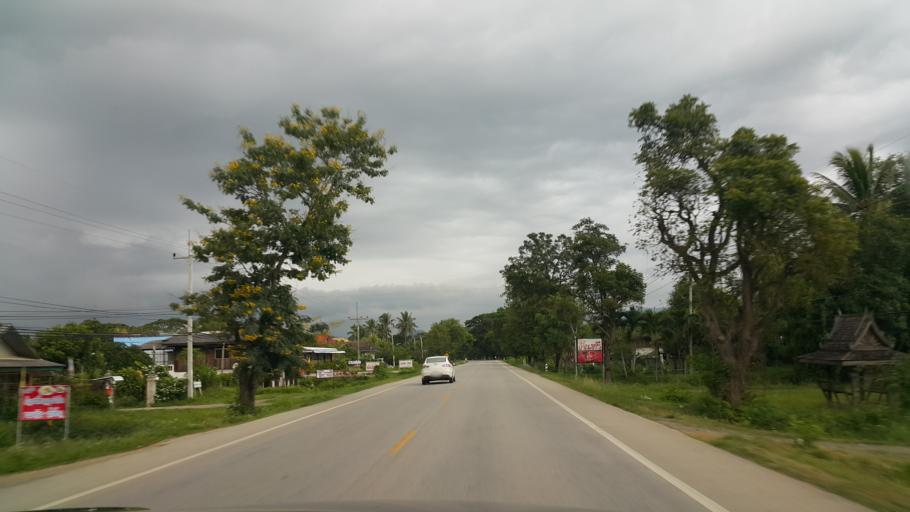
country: TH
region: Phayao
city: Dok Kham Tai
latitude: 19.1988
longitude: 100.0301
